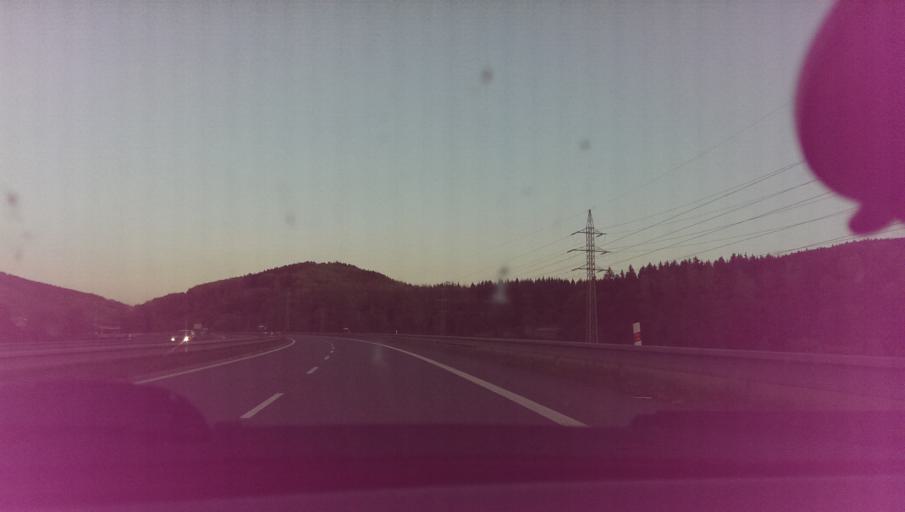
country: CZ
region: Zlin
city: Jablunka
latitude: 49.3653
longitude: 17.9469
